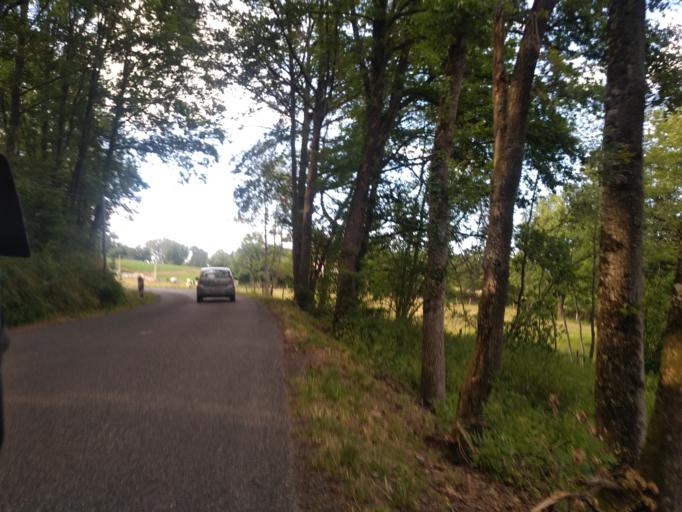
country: FR
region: Rhone-Alpes
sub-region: Departement du Rhone
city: Haute-Rivoire
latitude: 45.7395
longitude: 4.3509
